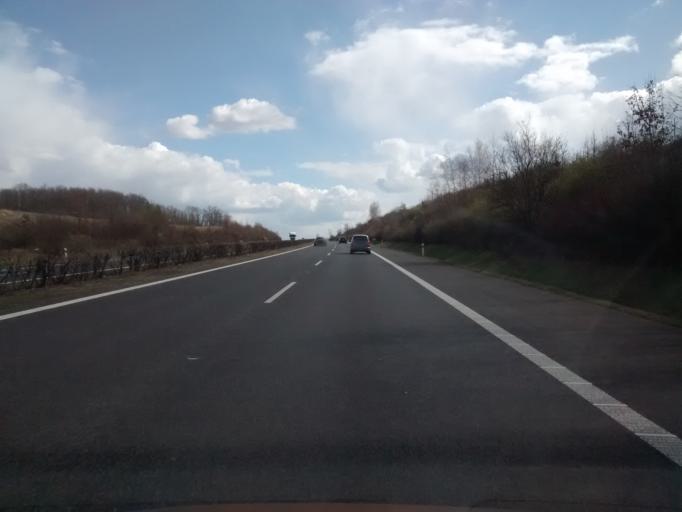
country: CZ
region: Ustecky
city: Roudnice nad Labem
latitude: 50.3689
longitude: 14.2559
